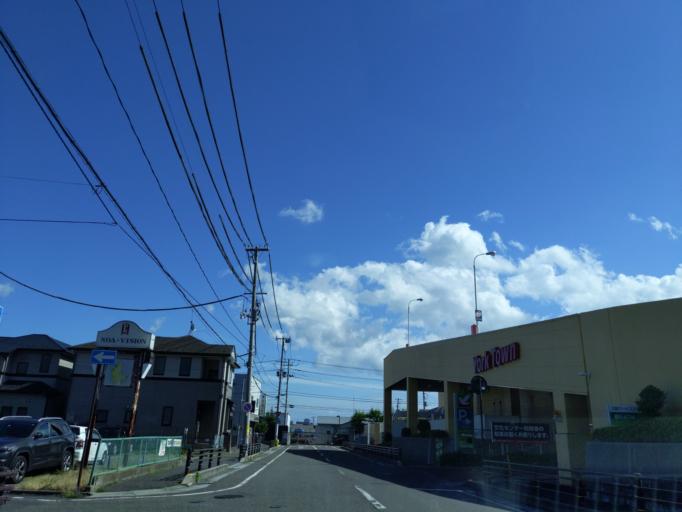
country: JP
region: Fukushima
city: Koriyama
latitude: 37.3910
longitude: 140.3789
